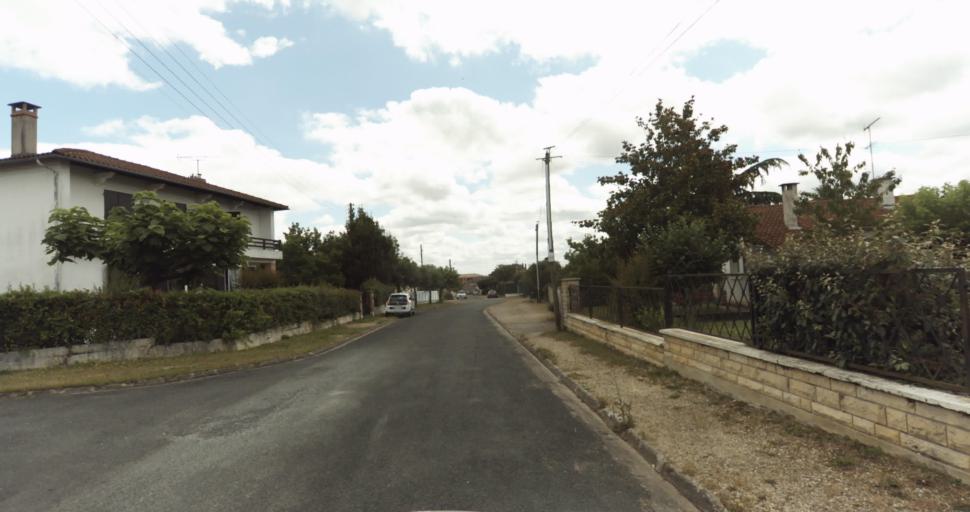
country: FR
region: Aquitaine
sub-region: Departement de la Gironde
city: Bazas
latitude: 44.4366
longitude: -0.2210
